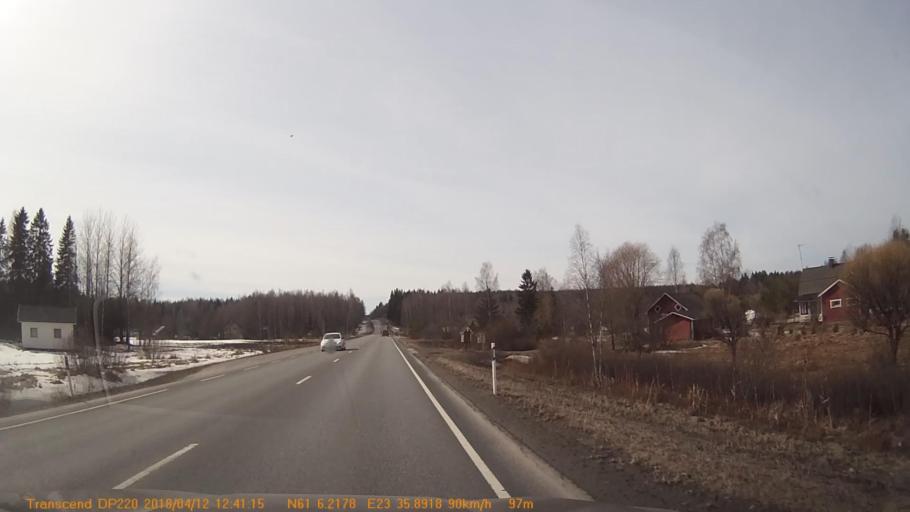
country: FI
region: Pirkanmaa
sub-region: Etelae-Pirkanmaa
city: Urjala
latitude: 61.1036
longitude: 23.5980
